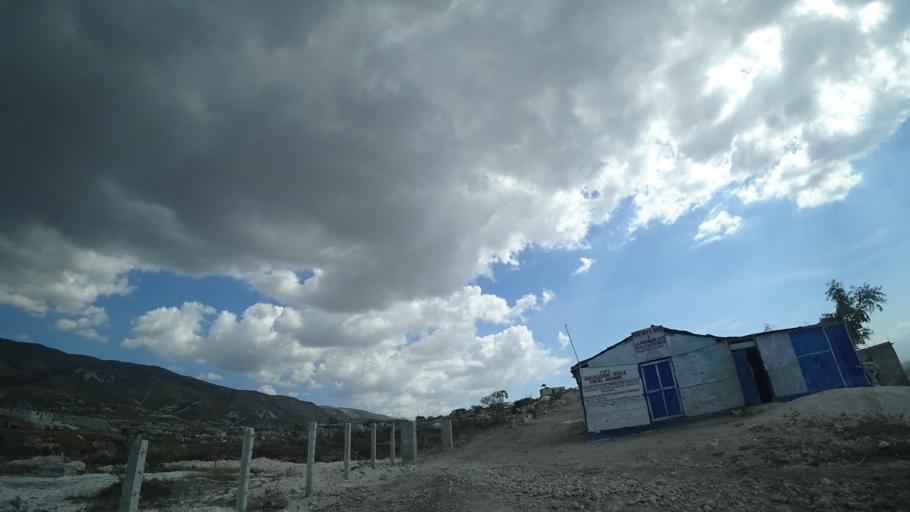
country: HT
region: Ouest
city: Cabaret
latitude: 18.6788
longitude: -72.3140
